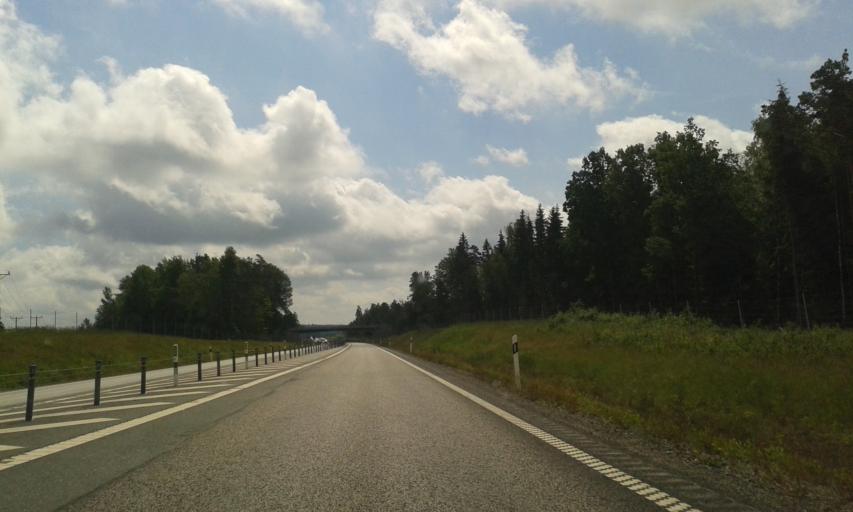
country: SE
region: Joenkoeping
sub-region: Gislaveds Kommun
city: Gislaved
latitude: 57.2929
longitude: 13.5923
